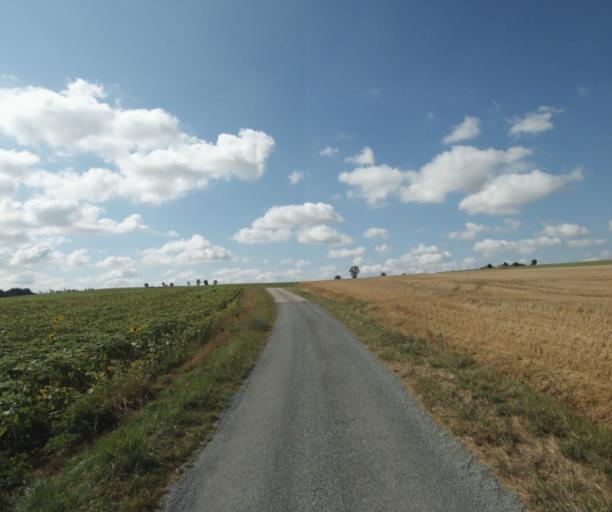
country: FR
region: Midi-Pyrenees
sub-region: Departement de la Haute-Garonne
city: Avignonet-Lauragais
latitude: 43.4449
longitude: 1.7977
